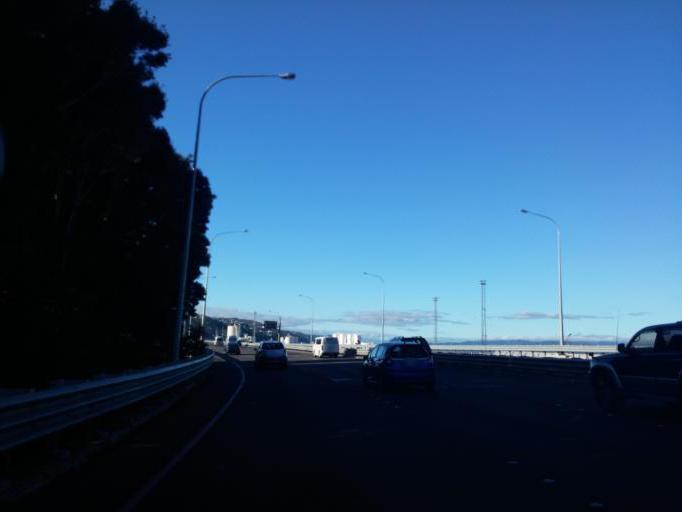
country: NZ
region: Wellington
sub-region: Wellington City
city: Wellington
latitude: -41.2702
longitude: 174.7803
